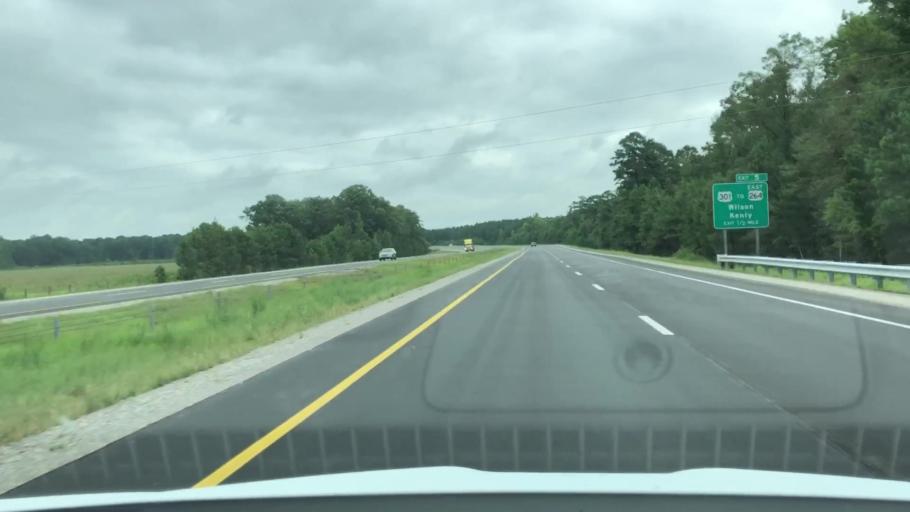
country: US
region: North Carolina
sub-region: Wilson County
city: Lucama
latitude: 35.6568
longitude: -77.9577
